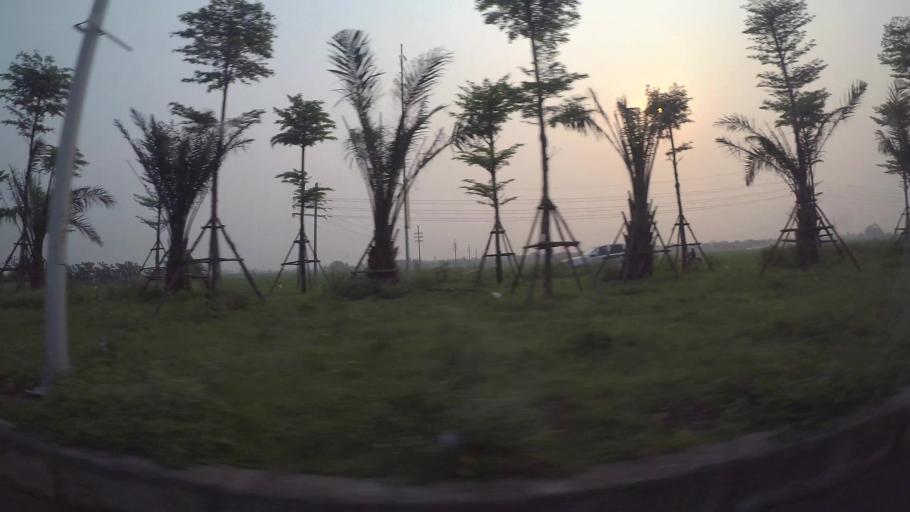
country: VN
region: Ha Noi
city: Kim Bai
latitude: 20.8850
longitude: 105.7976
